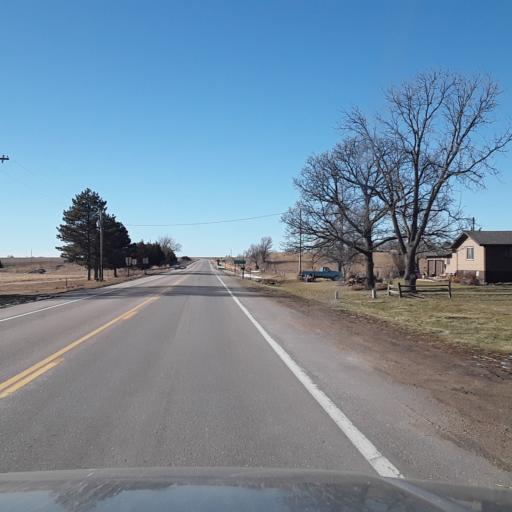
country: US
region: Nebraska
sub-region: Dawson County
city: Gothenburg
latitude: 40.7058
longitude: -100.2180
